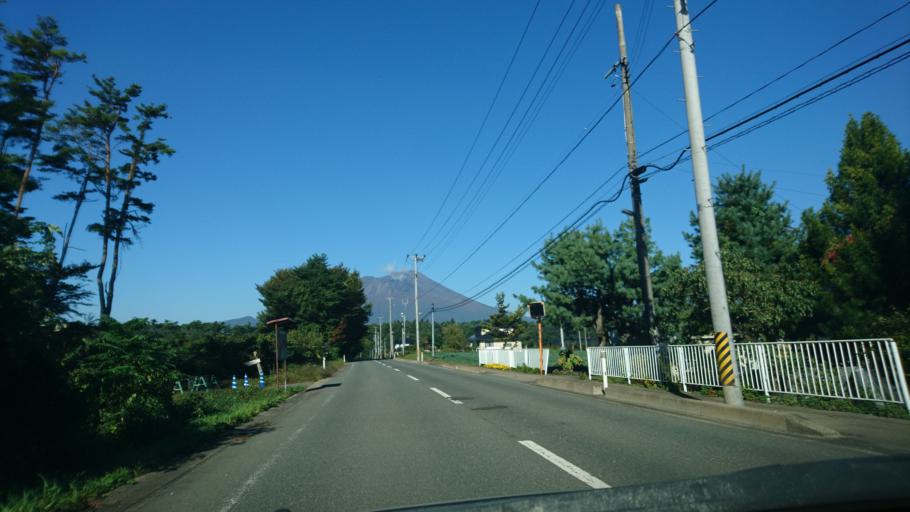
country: JP
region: Iwate
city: Morioka-shi
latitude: 39.8108
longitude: 141.1347
